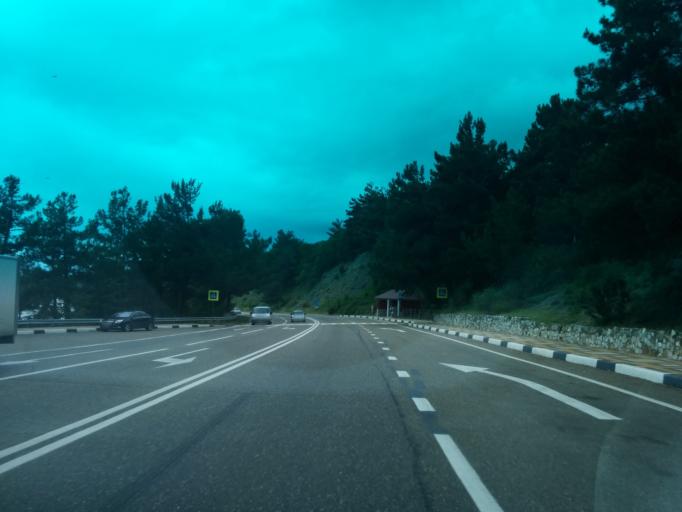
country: RU
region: Krasnodarskiy
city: Ol'ginka
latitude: 44.1836
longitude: 38.9264
